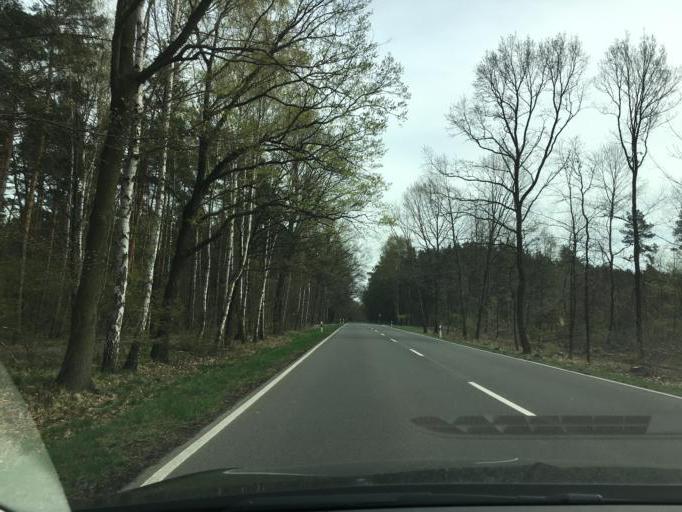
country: DE
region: Saxony
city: Schleife
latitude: 51.5736
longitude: 14.5051
